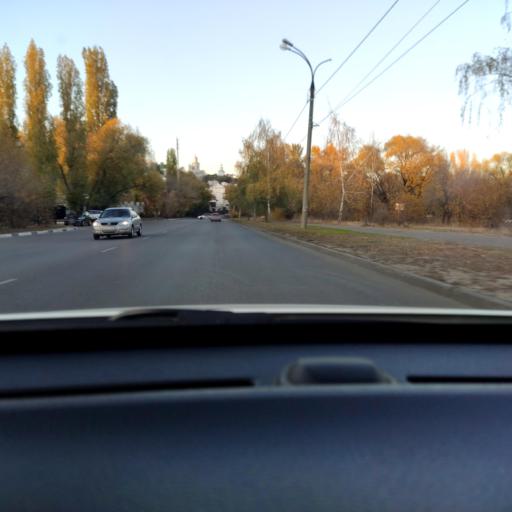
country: RU
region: Voronezj
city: Voronezh
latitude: 51.6535
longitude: 39.2121
